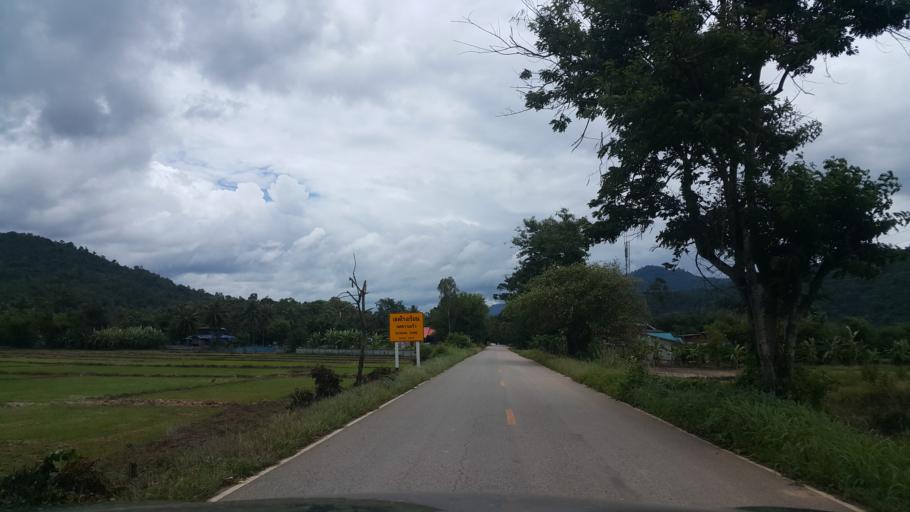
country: TH
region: Phitsanulok
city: Chat Trakan
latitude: 17.3832
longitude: 100.7538
